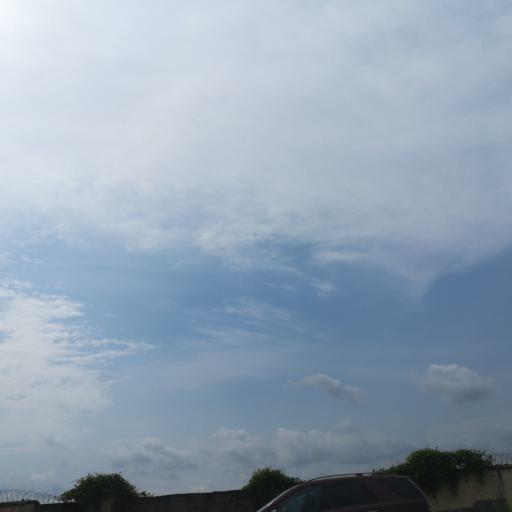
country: NG
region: Rivers
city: Port Harcourt
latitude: 4.8487
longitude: 7.0153
